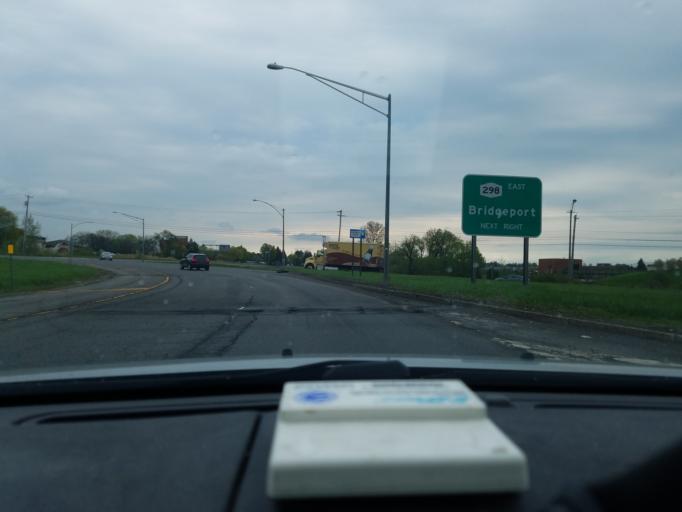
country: US
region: New York
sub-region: Onondaga County
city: East Syracuse
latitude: 43.0873
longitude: -76.0908
